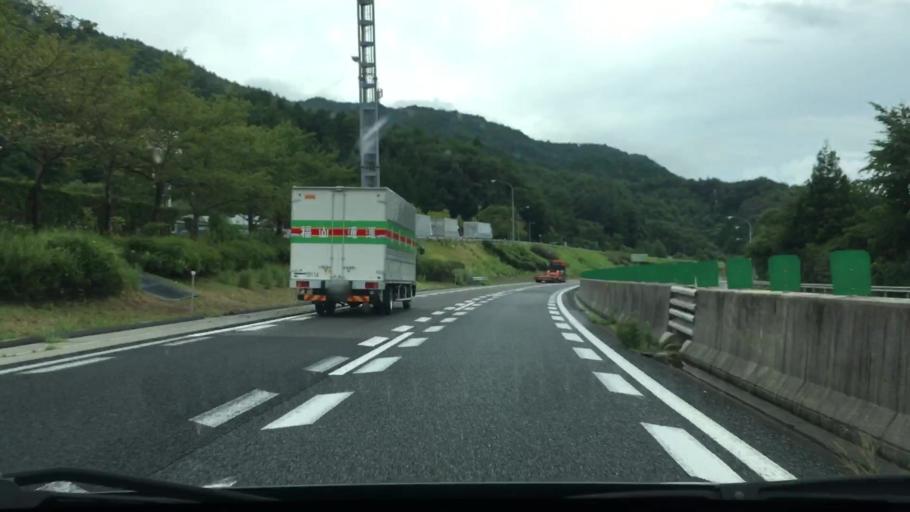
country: JP
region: Hiroshima
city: Hiroshima-shi
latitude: 34.5895
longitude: 132.4846
